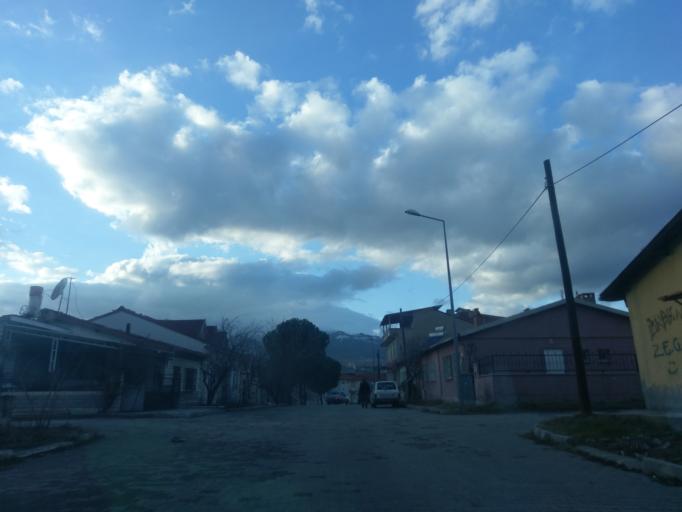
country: TR
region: Kuetahya
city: Gediz
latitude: 38.9920
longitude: 29.3878
